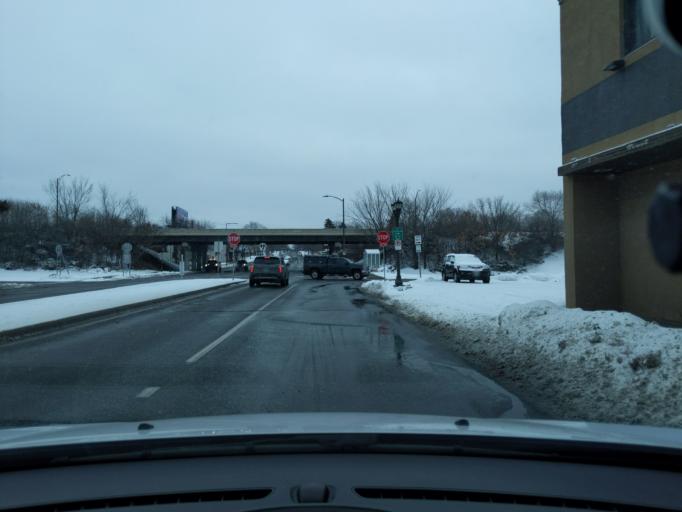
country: US
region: Minnesota
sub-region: Ramsey County
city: Falcon Heights
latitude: 44.9773
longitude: -93.1683
